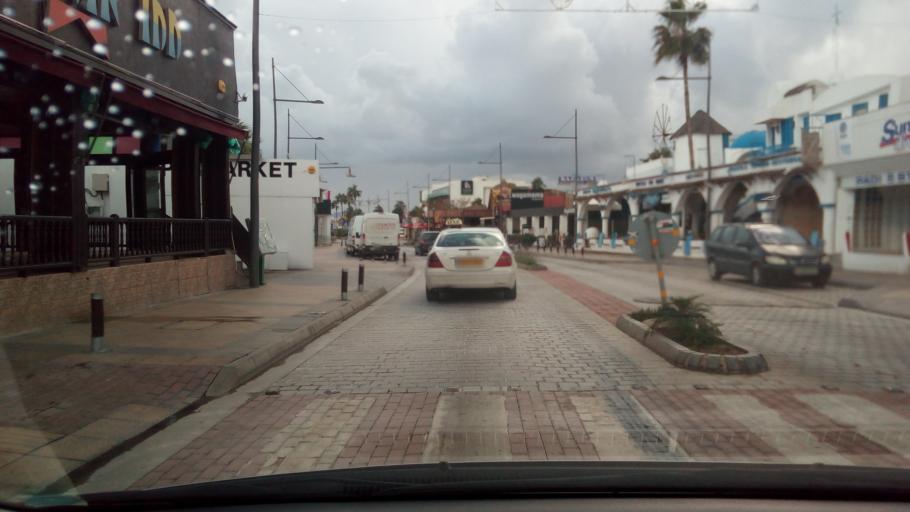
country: CY
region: Ammochostos
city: Ayia Napa
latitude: 34.9856
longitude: 34.0004
